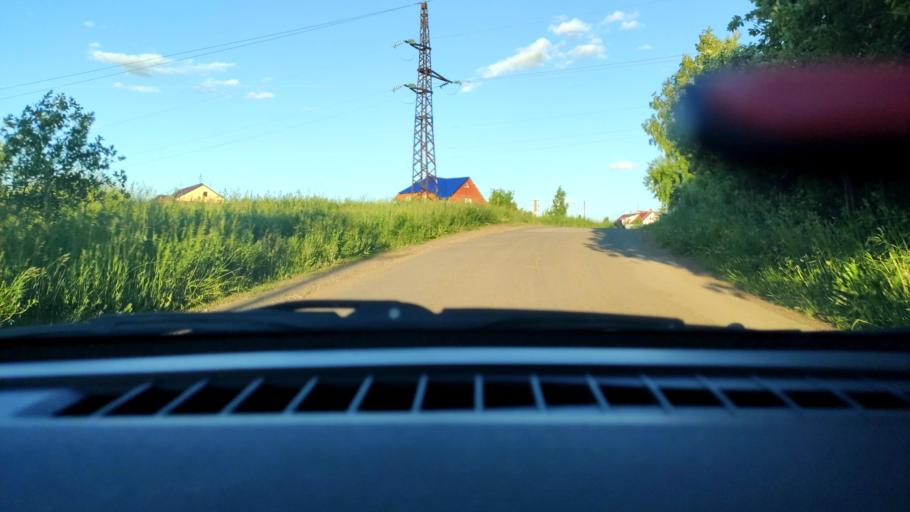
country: RU
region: Perm
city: Kultayevo
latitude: 57.9363
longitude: 55.8638
